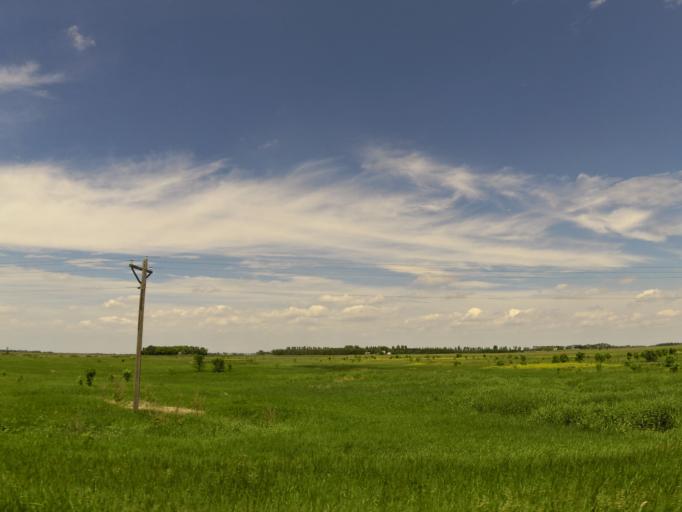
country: US
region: North Dakota
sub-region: Walsh County
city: Grafton
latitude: 48.2953
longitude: -97.1970
